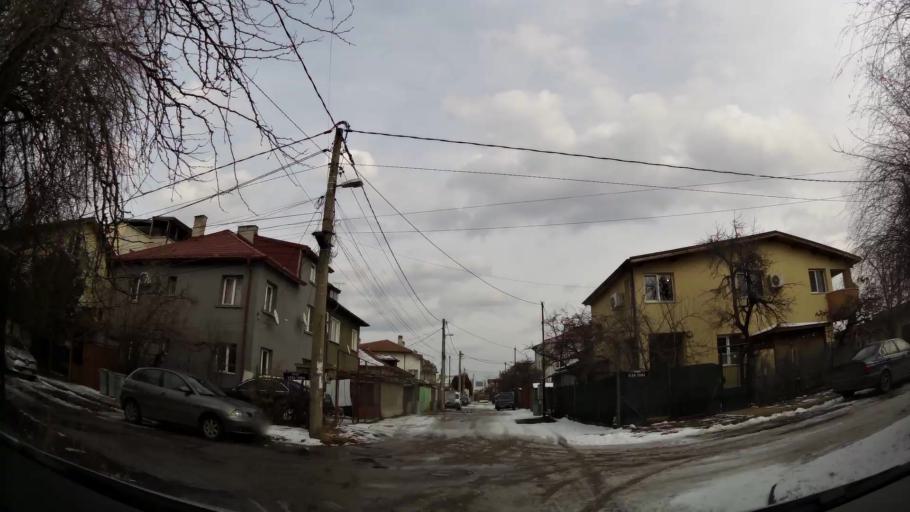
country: BG
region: Sofia-Capital
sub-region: Stolichna Obshtina
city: Sofia
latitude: 42.7033
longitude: 23.3837
